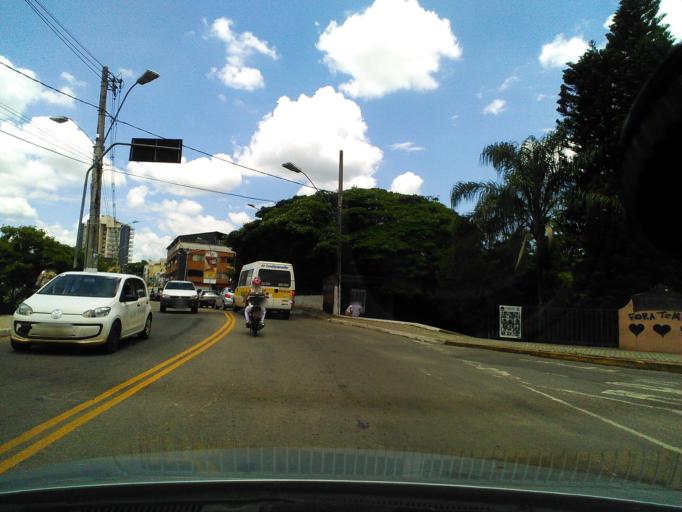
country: BR
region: Minas Gerais
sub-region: Tres Coracoes
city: Tres Coracoes
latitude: -21.6998
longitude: -45.2598
